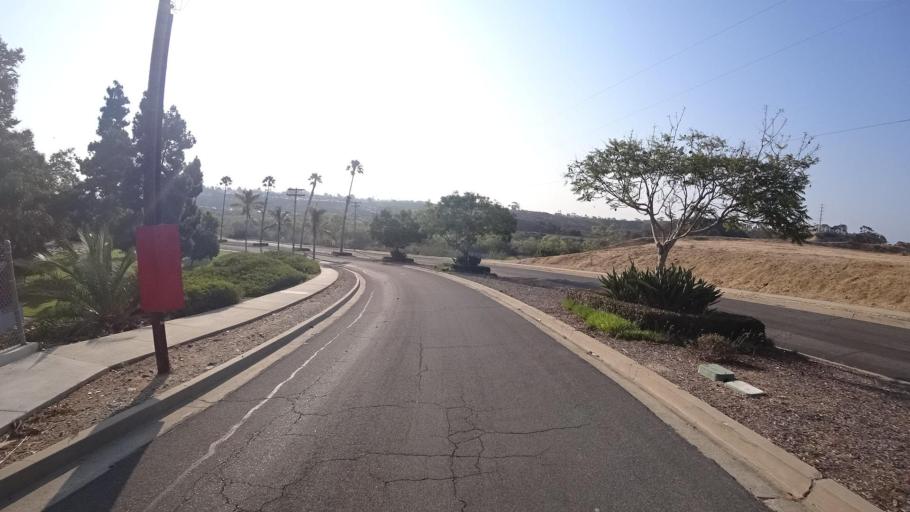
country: US
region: California
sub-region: San Diego County
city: Oceanside
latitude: 33.2110
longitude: -117.3817
